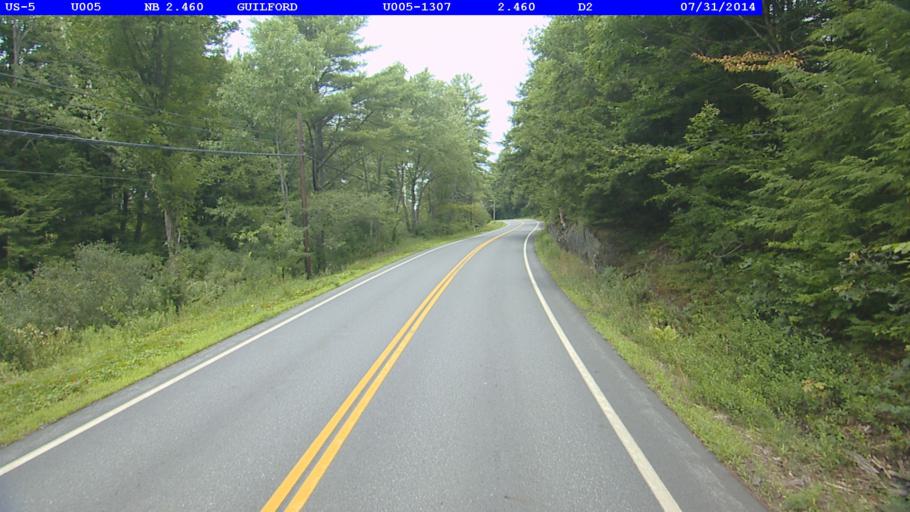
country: US
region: New Hampshire
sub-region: Cheshire County
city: Hinsdale
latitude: 42.7648
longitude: -72.5685
